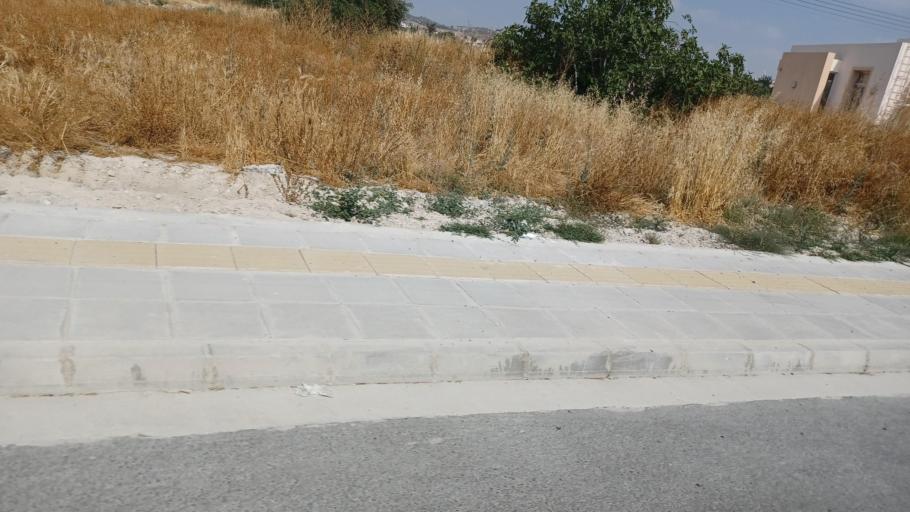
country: CY
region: Larnaka
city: Aradippou
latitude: 34.9256
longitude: 33.5372
